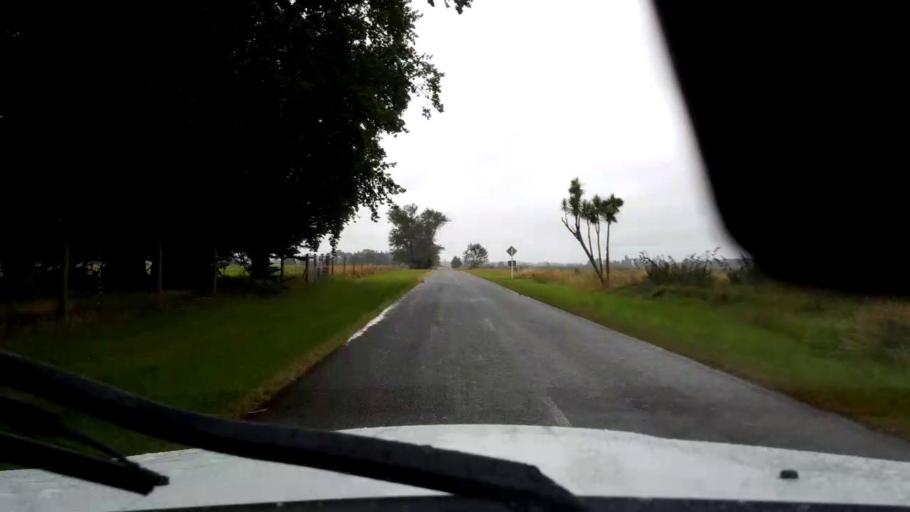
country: NZ
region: Canterbury
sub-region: Timaru District
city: Pleasant Point
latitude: -44.2518
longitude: 171.2215
